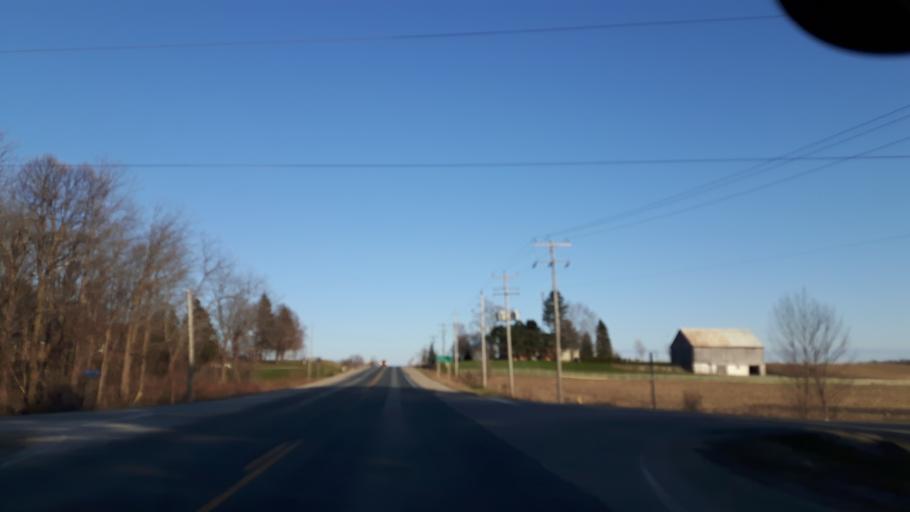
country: CA
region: Ontario
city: Goderich
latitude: 43.7243
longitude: -81.6807
